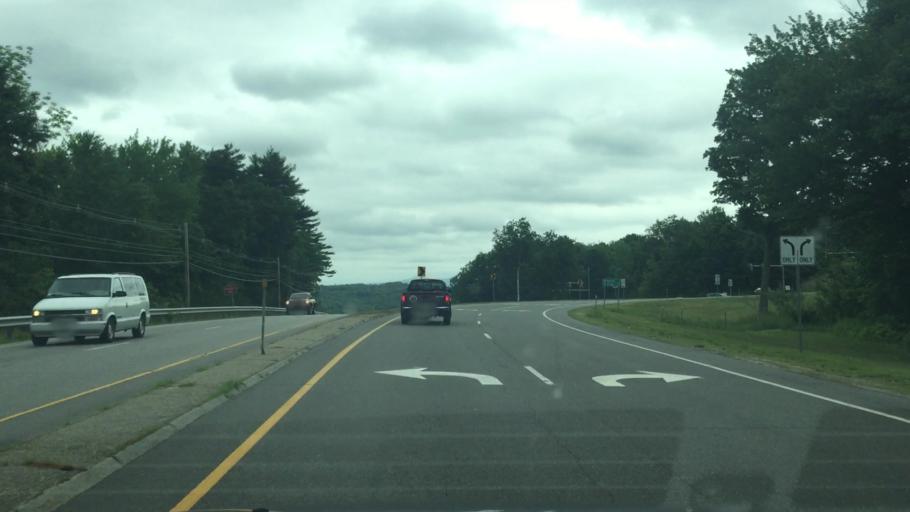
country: US
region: New Hampshire
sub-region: Belknap County
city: Meredith
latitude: 43.6450
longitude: -71.5030
